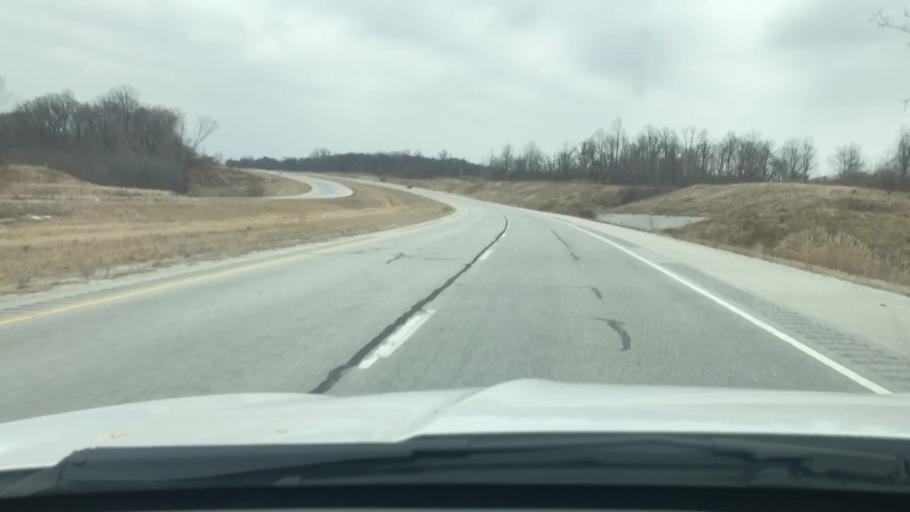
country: US
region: Indiana
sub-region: Carroll County
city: Flora
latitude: 40.6463
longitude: -86.5682
